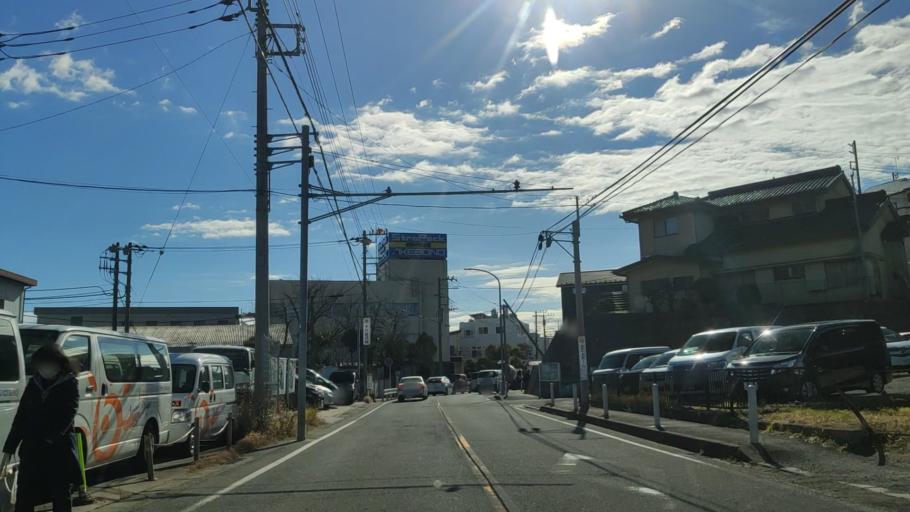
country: JP
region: Kanagawa
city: Yokohama
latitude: 35.4975
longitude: 139.6022
